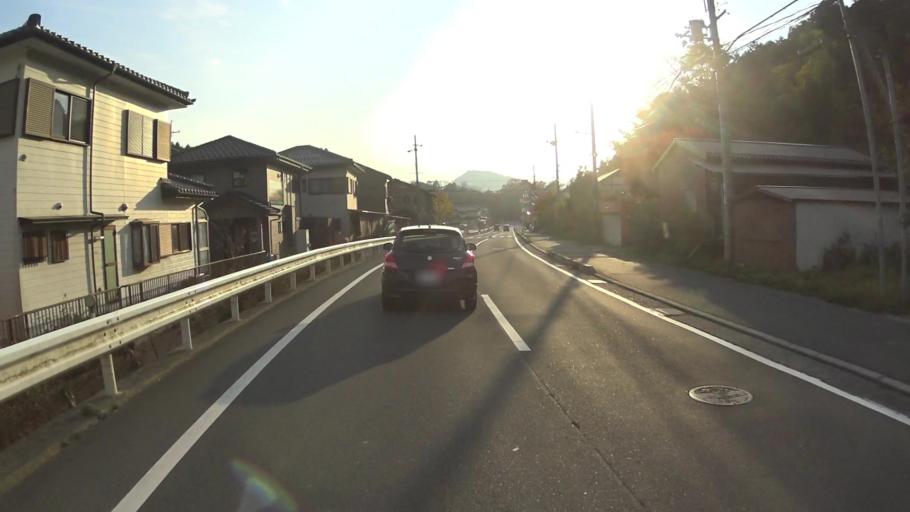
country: JP
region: Kyoto
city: Maizuru
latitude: 35.4878
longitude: 135.4365
